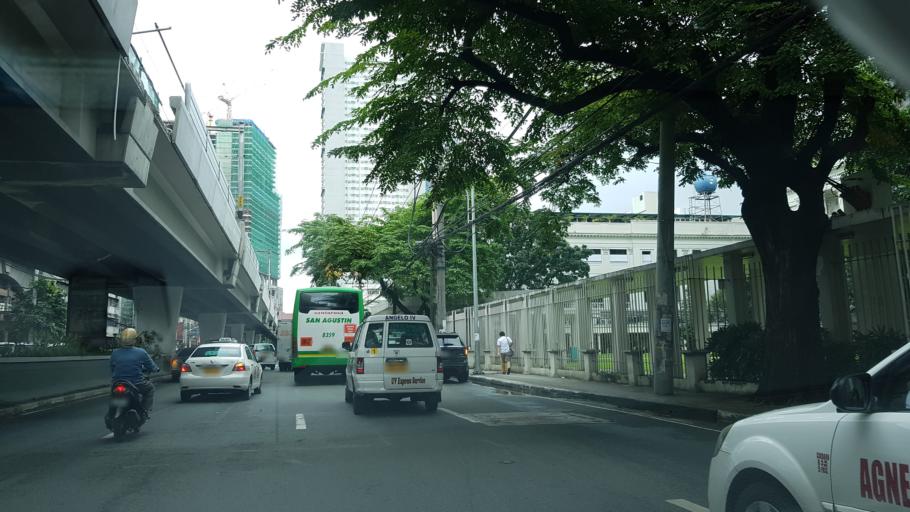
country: PH
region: Metro Manila
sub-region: City of Manila
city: Port Area
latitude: 14.5657
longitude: 120.9937
